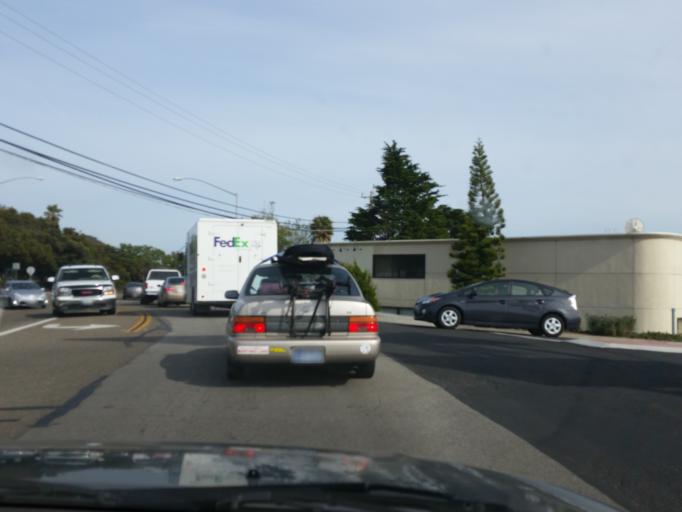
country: US
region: California
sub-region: San Luis Obispo County
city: Pismo Beach
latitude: 35.1467
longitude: -120.6456
